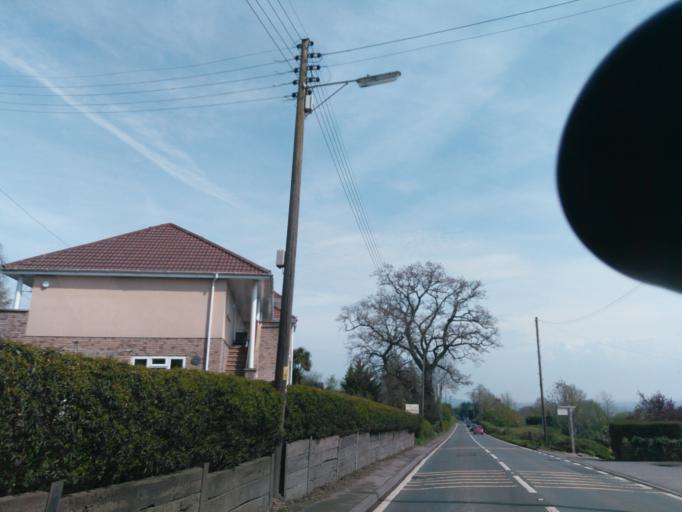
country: GB
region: England
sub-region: Somerset
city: Glastonbury
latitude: 51.1416
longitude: -2.6999
